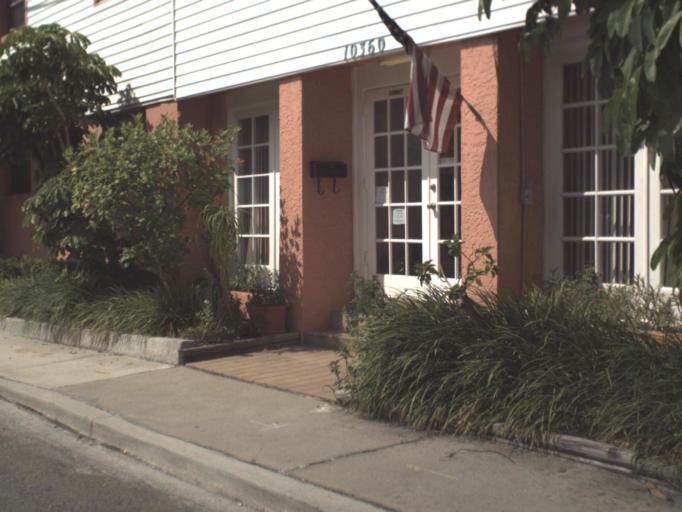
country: US
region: Florida
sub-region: Pinellas County
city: Treasure Island
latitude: 27.7659
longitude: -82.7681
